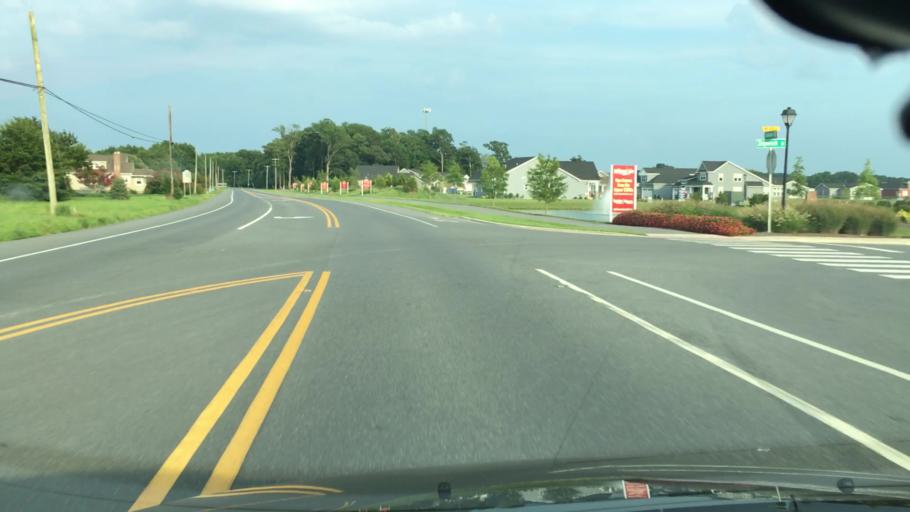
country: US
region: Delaware
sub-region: Sussex County
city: Selbyville
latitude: 38.4643
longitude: -75.1658
